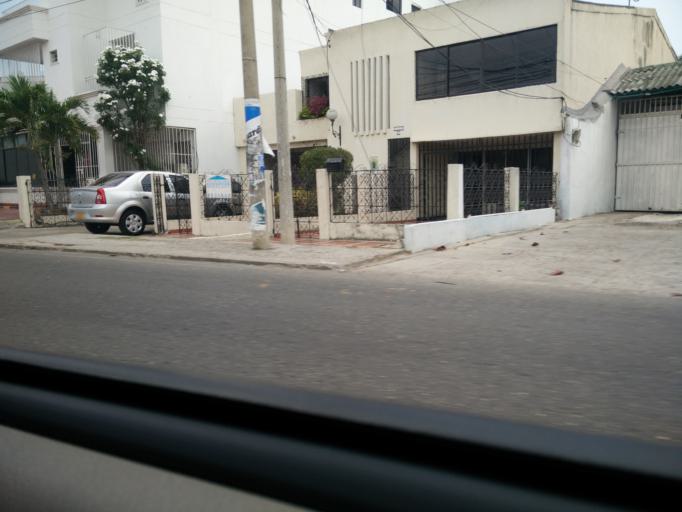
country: CO
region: Bolivar
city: Cartagena
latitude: 10.4430
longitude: -75.5206
